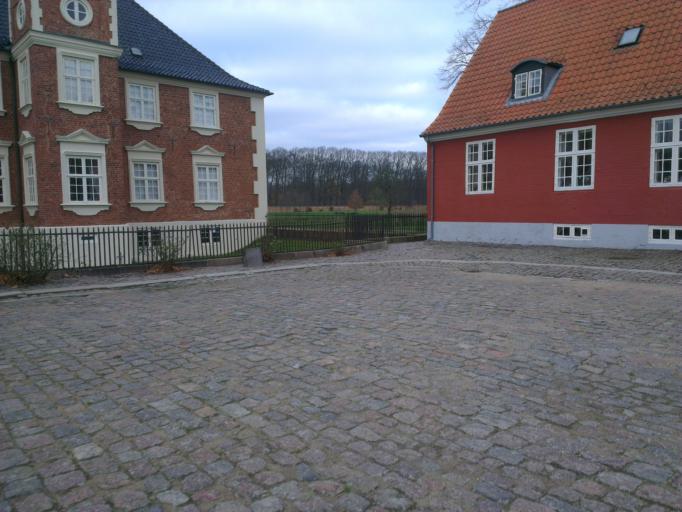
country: DK
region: Capital Region
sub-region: Frederikssund Kommune
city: Jaegerspris
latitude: 55.8561
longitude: 11.9744
